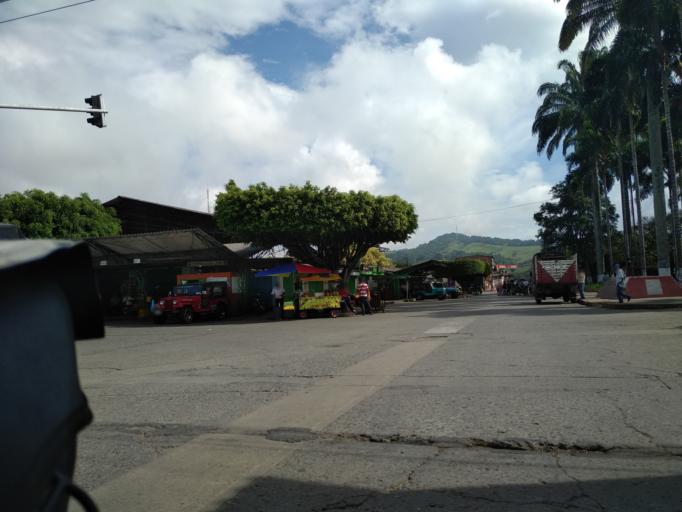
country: CO
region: Valle del Cauca
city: Caicedonia
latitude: 4.3344
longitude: -75.8291
